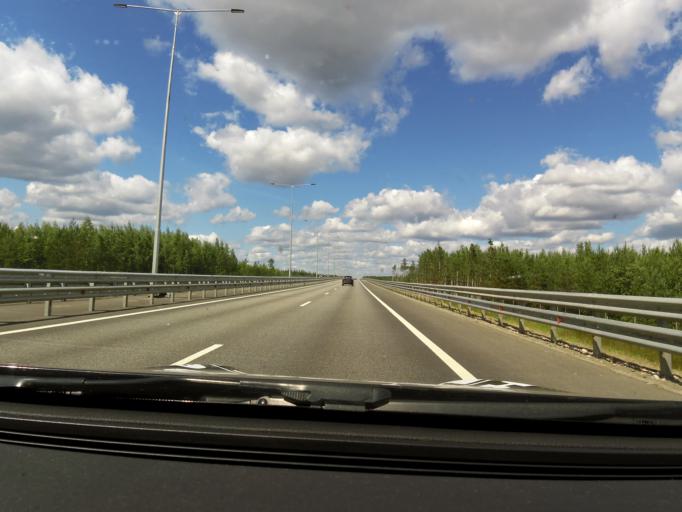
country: RU
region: Tverskaya
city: Krasnomayskiy
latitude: 57.4637
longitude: 34.3750
